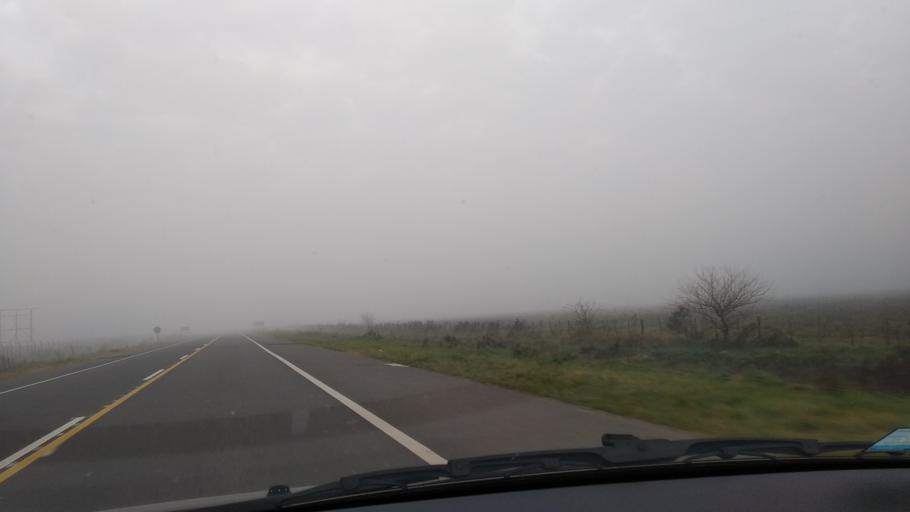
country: AR
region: Buenos Aires
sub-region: Partido de San Vicente
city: San Vicente
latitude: -35.2182
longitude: -58.4304
